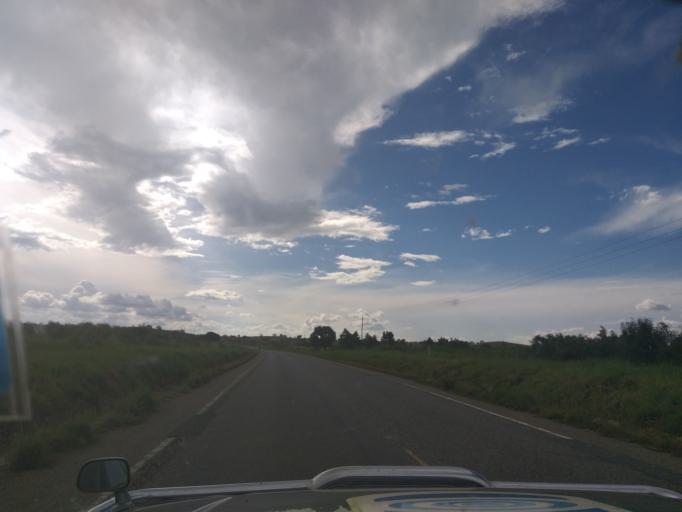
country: UG
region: Northern Region
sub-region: Nebbi District
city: Nebbi
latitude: 2.4638
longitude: 31.3030
